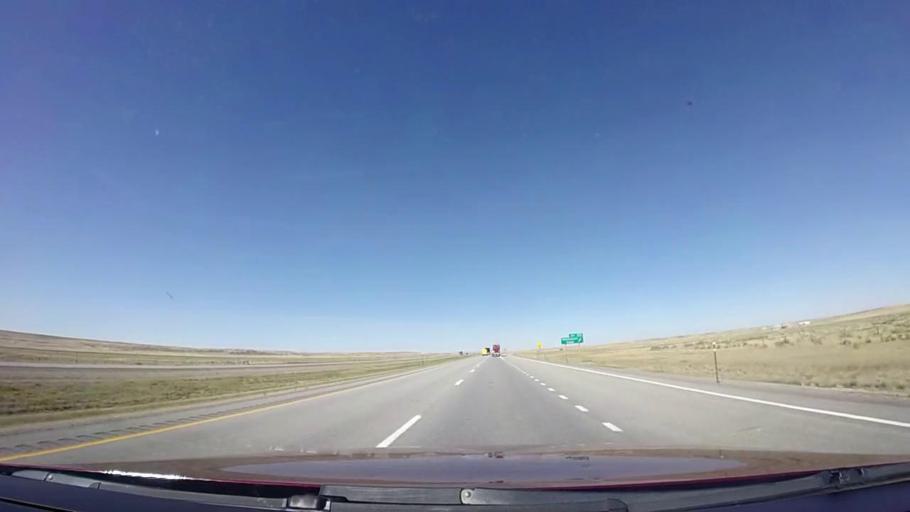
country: US
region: Wyoming
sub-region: Carbon County
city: Rawlins
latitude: 41.6664
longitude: -108.0254
